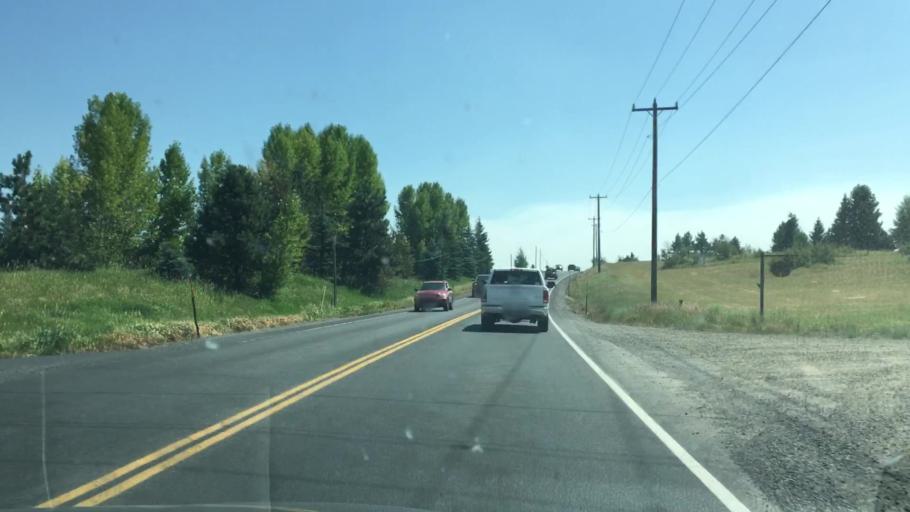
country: US
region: Idaho
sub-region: Valley County
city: McCall
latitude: 44.8833
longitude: -116.0908
